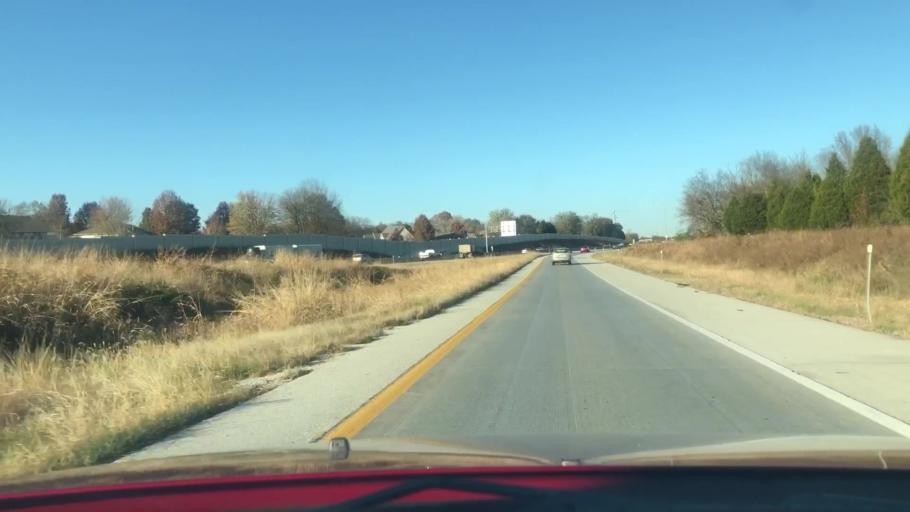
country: US
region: Missouri
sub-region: Greene County
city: Springfield
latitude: 37.1313
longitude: -93.2277
